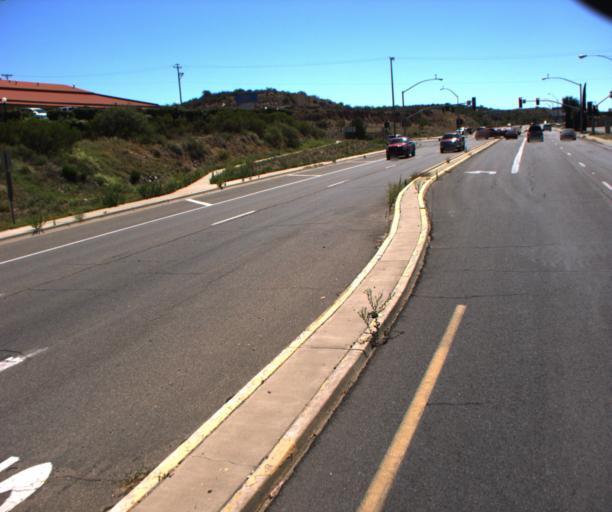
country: US
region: Arizona
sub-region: Gila County
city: Globe
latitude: 33.3929
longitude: -110.7665
